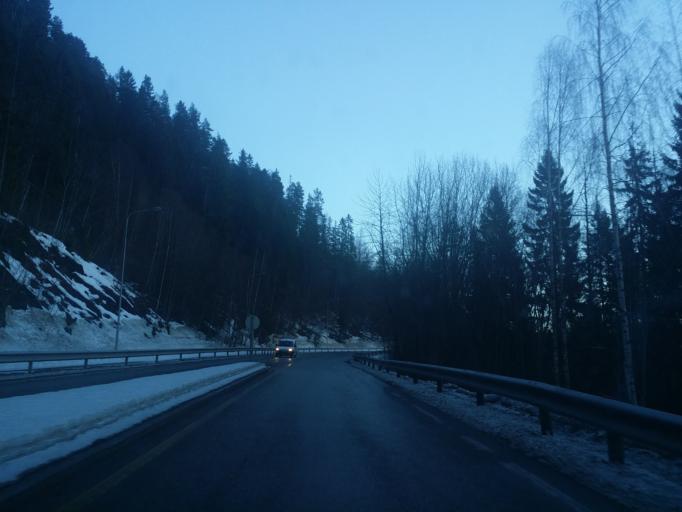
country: NO
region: Buskerud
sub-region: Hole
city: Vik
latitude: 59.9964
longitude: 10.2891
